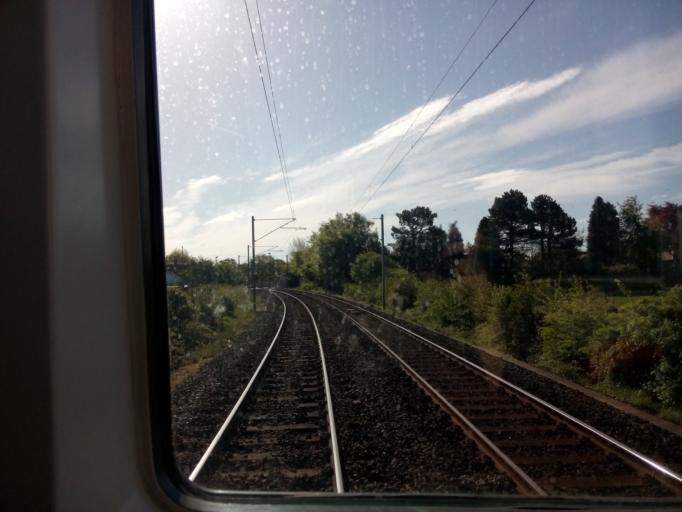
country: GB
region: England
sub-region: Newcastle upon Tyne
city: Dinnington
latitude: 55.0146
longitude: -1.6812
